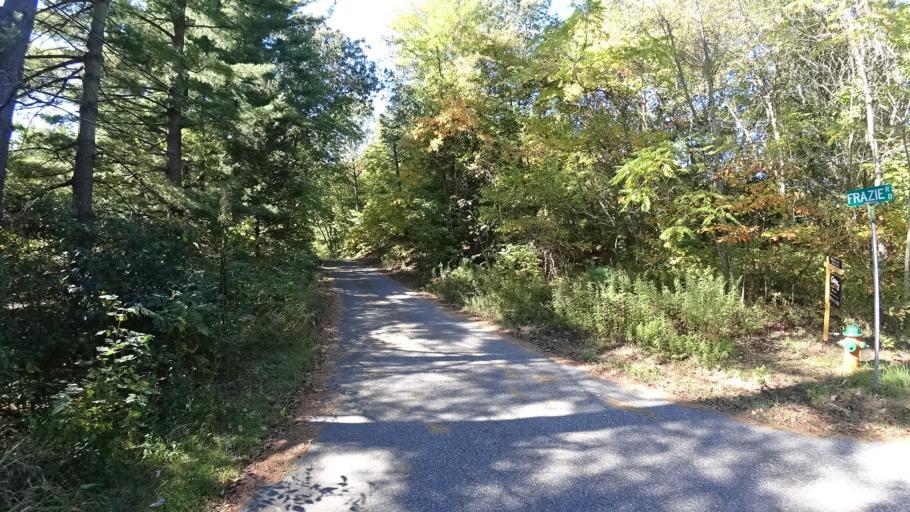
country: US
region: Indiana
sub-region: LaPorte County
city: Long Beach
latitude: 41.7452
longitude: -86.8162
